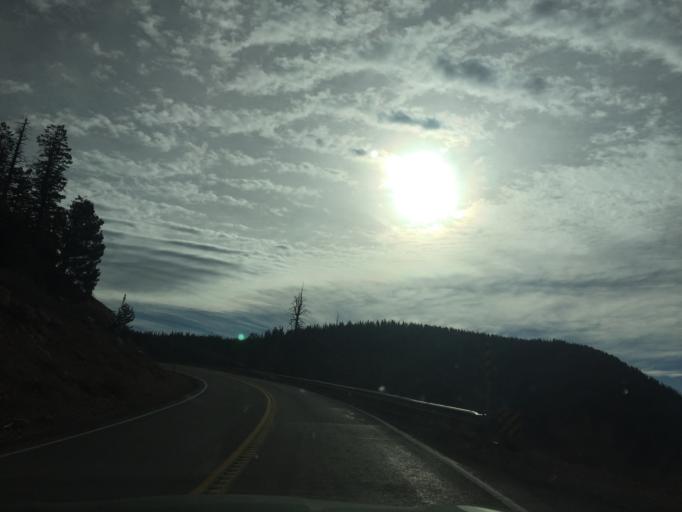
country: US
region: Utah
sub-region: Iron County
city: Cedar City
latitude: 37.5706
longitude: -112.8583
